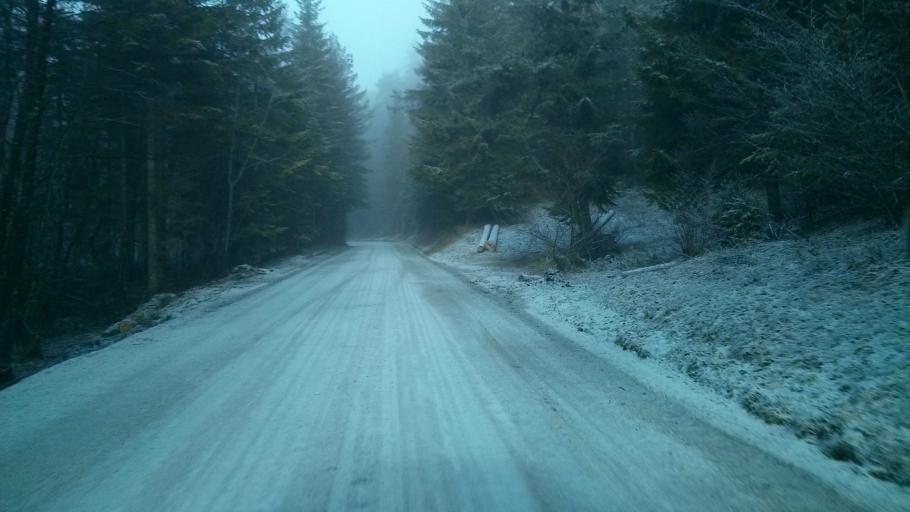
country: SI
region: Zagorje ob Savi
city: Zagorje ob Savi
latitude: 46.0531
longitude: 14.9935
